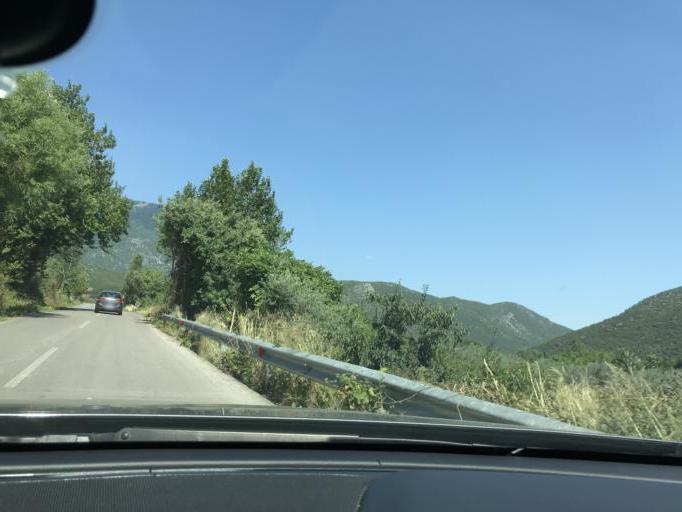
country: GR
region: Central Greece
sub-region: Nomos Fthiotidos
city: Kato Tithorea
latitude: 38.5202
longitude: 22.7443
